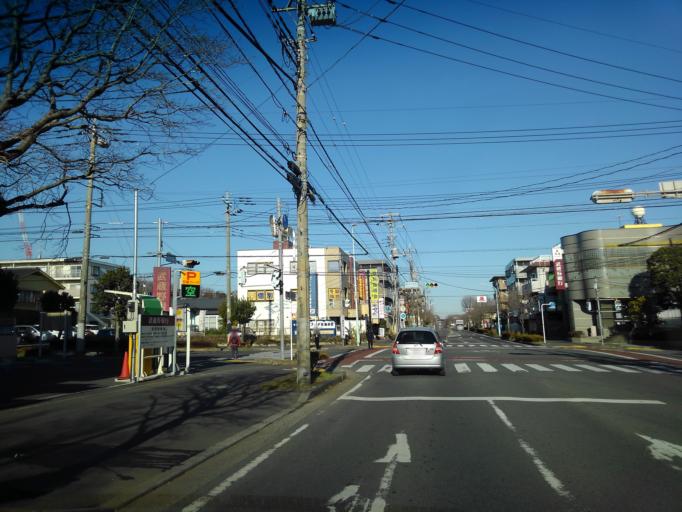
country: JP
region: Saitama
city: Tokorozawa
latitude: 35.7967
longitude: 139.5121
